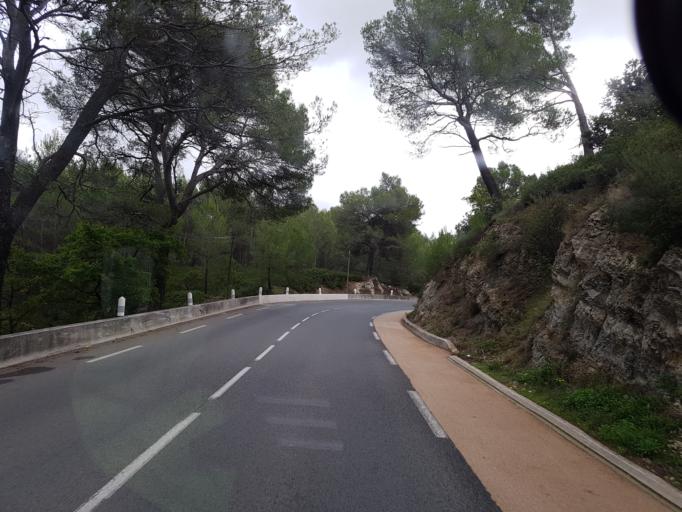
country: FR
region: Provence-Alpes-Cote d'Azur
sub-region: Departement des Bouches-du-Rhone
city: Cuges-les-Pins
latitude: 43.2682
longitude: 5.7370
